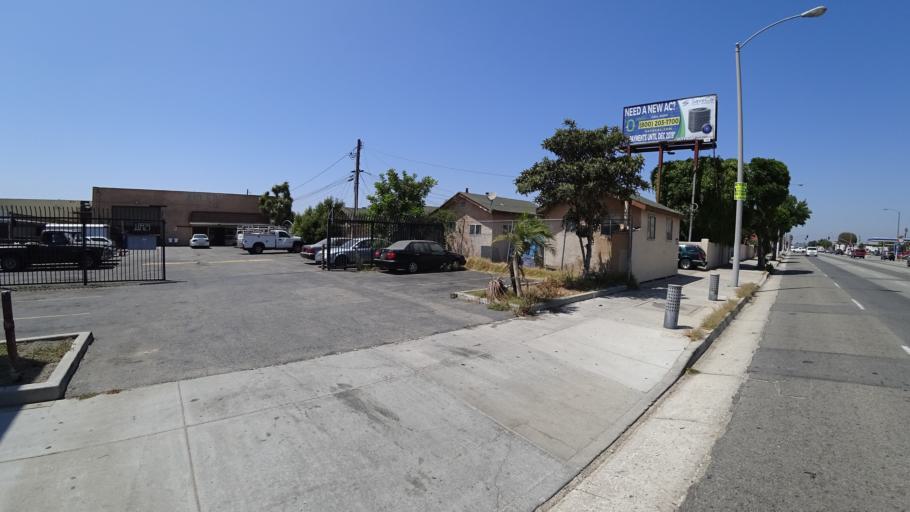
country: US
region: California
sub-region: Los Angeles County
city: Lennox
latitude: 33.9359
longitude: -118.3440
